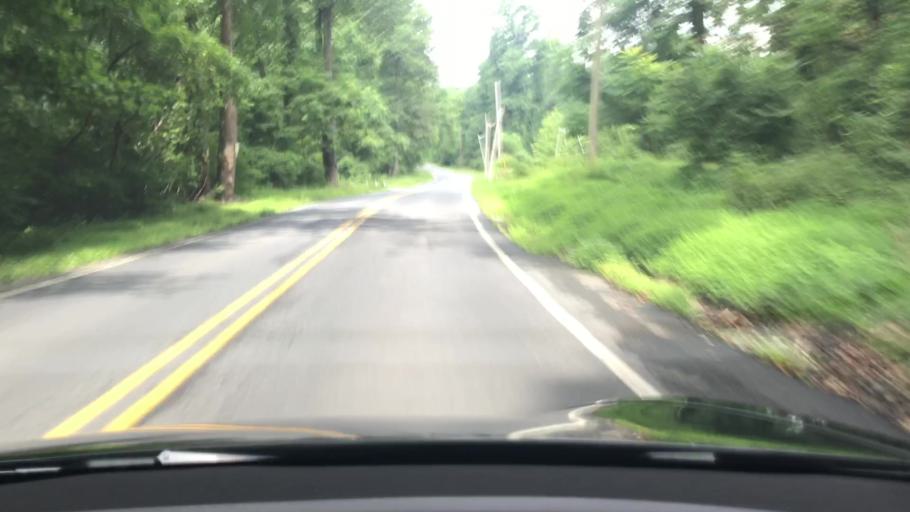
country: US
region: Pennsylvania
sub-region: Cumberland County
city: New Cumberland
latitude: 40.1916
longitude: -76.8745
